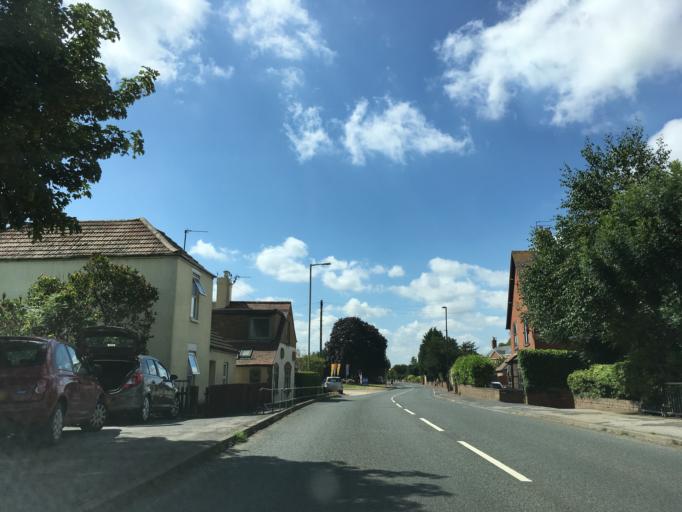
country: GB
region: England
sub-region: Gloucestershire
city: Gloucester
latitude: 51.8895
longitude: -2.2338
